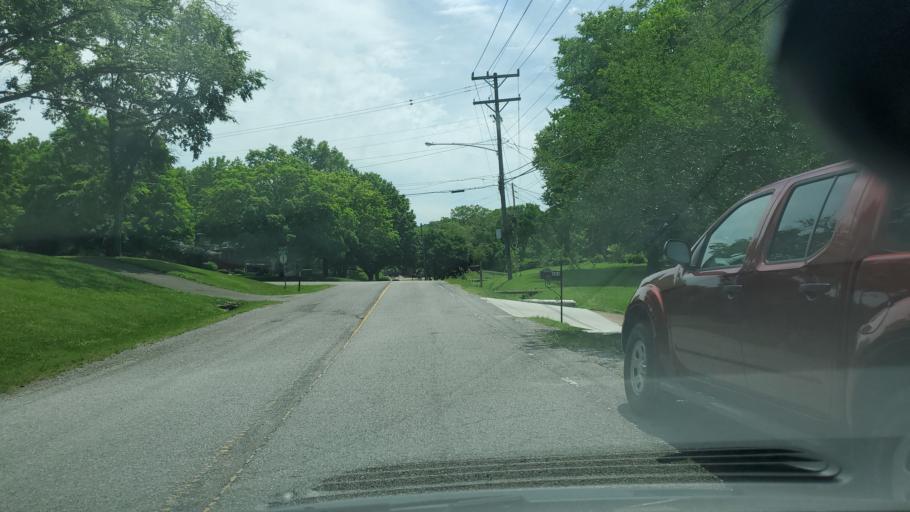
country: US
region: Tennessee
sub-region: Davidson County
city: Oak Hill
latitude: 36.1155
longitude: -86.7092
